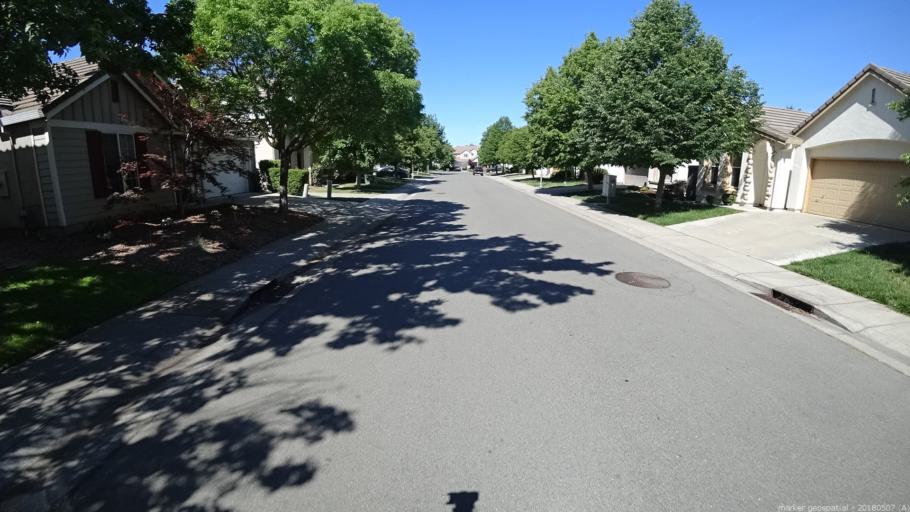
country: US
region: California
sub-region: Sacramento County
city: Rio Linda
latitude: 38.6575
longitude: -121.5010
